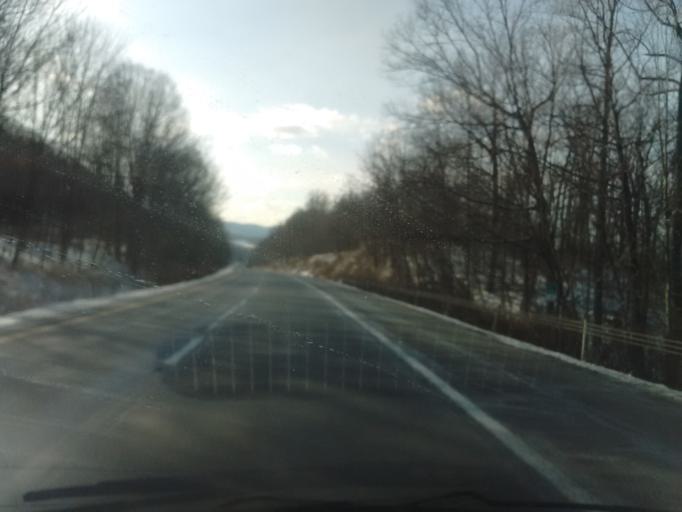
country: US
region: New York
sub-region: Dutchess County
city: Hillside Lake
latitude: 41.5476
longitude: -73.7445
